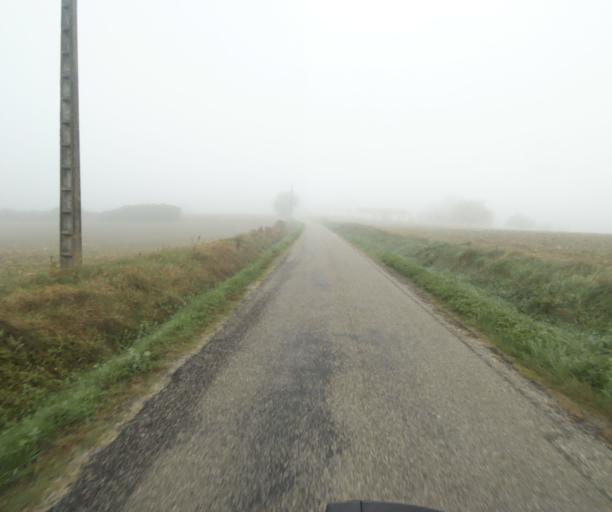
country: FR
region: Midi-Pyrenees
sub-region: Departement de la Haute-Garonne
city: Villemur-sur-Tarn
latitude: 43.9085
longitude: 1.4851
